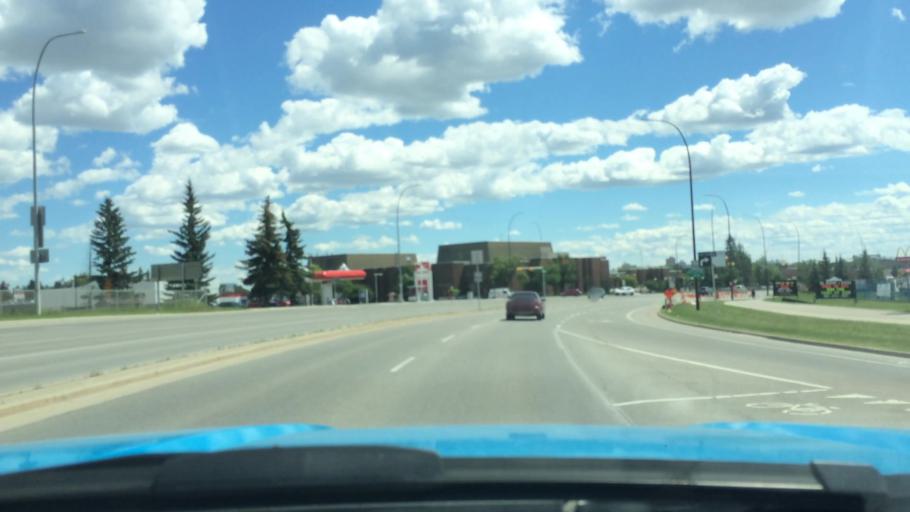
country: CA
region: Alberta
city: Calgary
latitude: 51.1022
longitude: -114.1423
